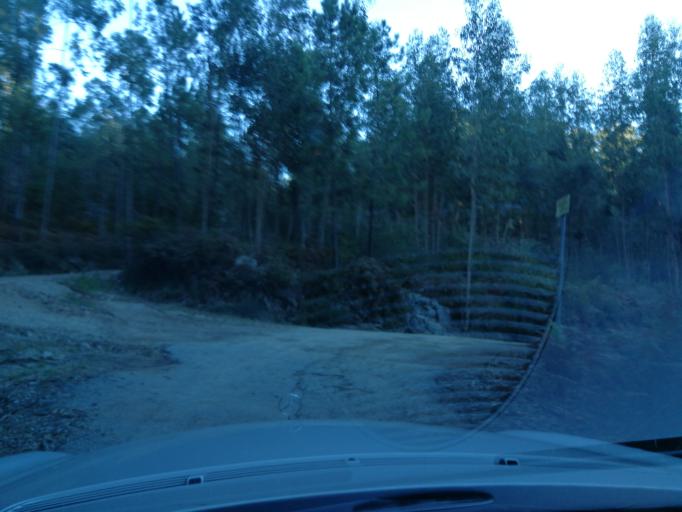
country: PT
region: Braga
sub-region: Braga
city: Oliveira
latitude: 41.4653
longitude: -8.4509
